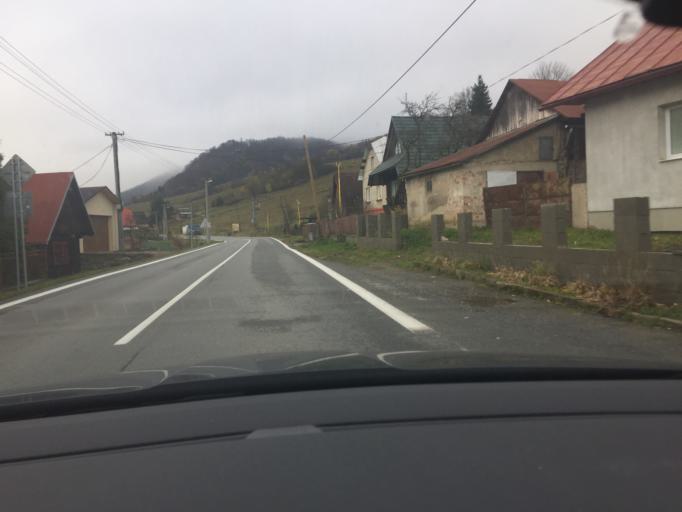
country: PL
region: Lesser Poland Voivodeship
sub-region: Powiat nowosadecki
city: Muszyna
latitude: 49.2975
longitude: 20.9373
